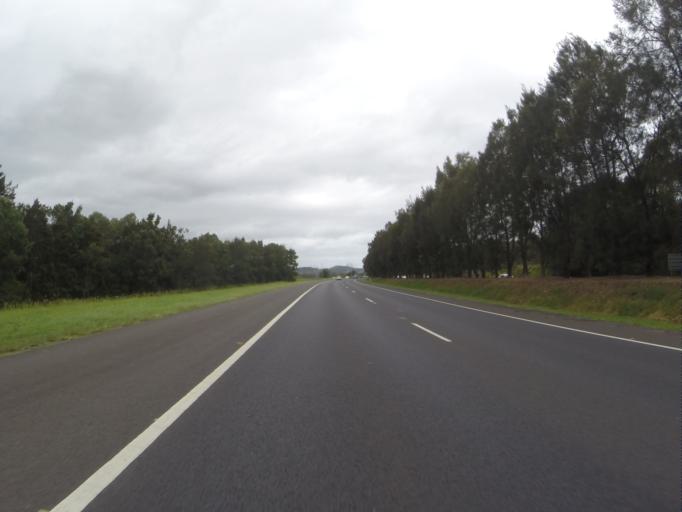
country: AU
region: New South Wales
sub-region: Wollongong
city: Koonawarra
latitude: -34.4873
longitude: 150.8092
